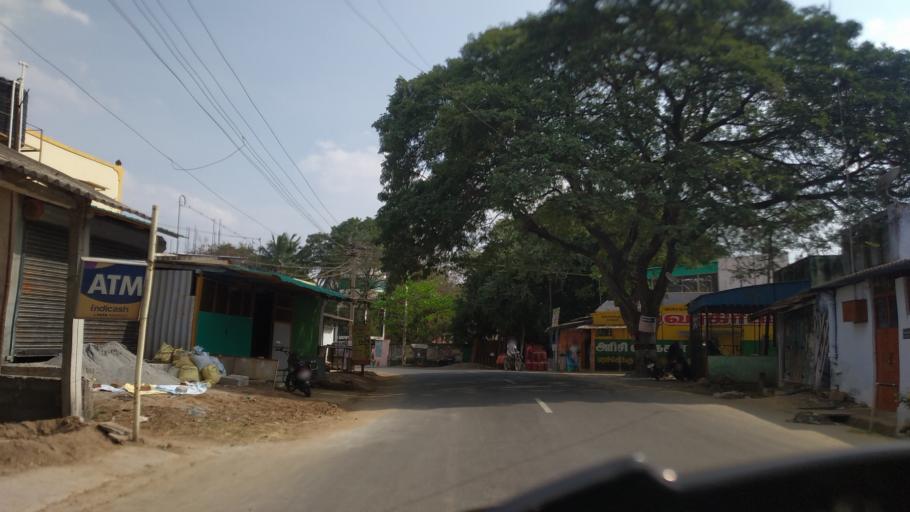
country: IN
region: Tamil Nadu
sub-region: Coimbatore
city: Perur
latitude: 10.9565
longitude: 76.7599
